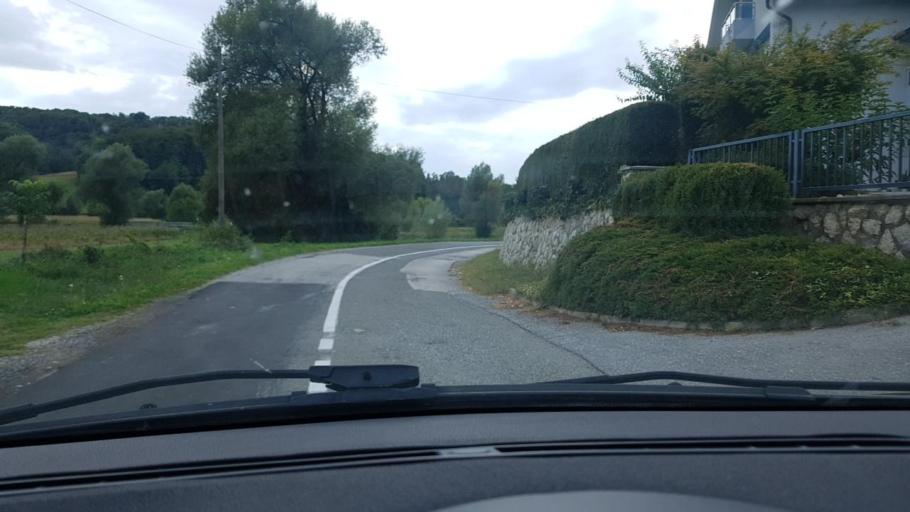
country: HR
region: Krapinsko-Zagorska
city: Pregrada
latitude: 46.1404
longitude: 15.7916
